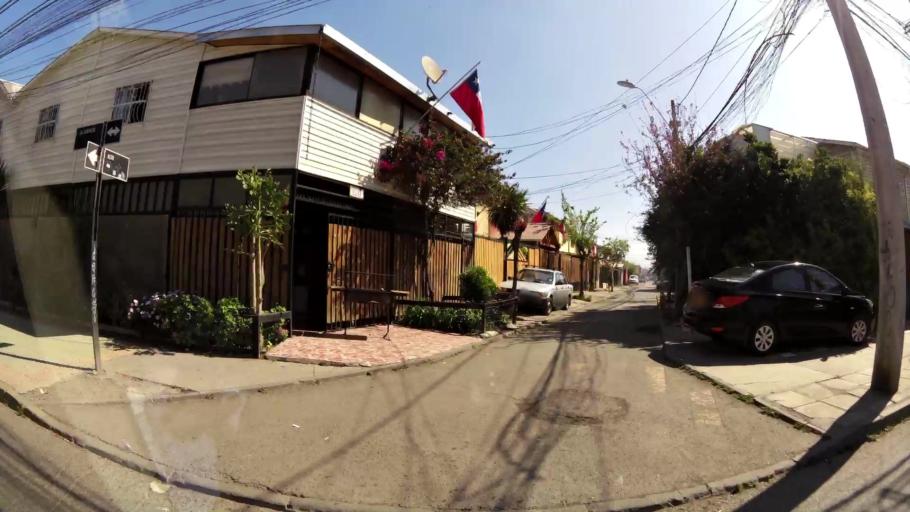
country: CL
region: Santiago Metropolitan
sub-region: Provincia de Santiago
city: Lo Prado
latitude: -33.3530
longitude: -70.7469
